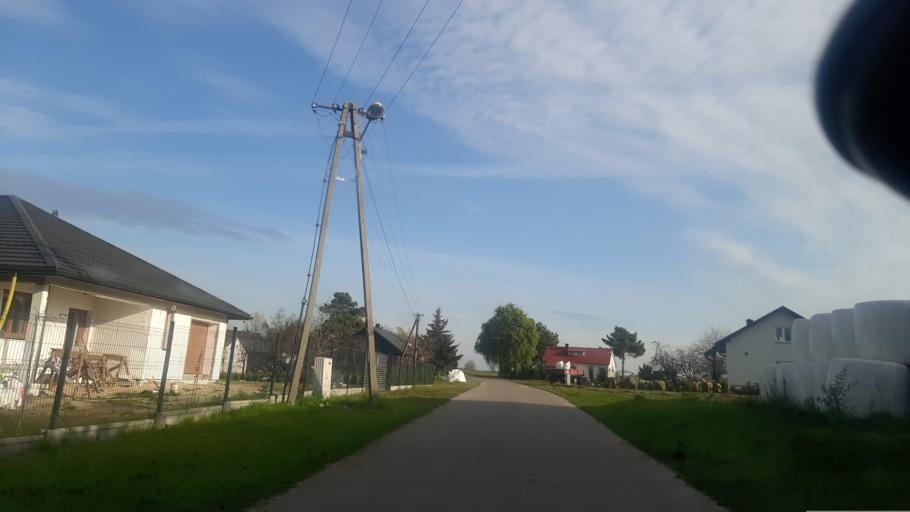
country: PL
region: Lublin Voivodeship
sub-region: Powiat pulawski
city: Markuszow
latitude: 51.3869
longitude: 22.2915
